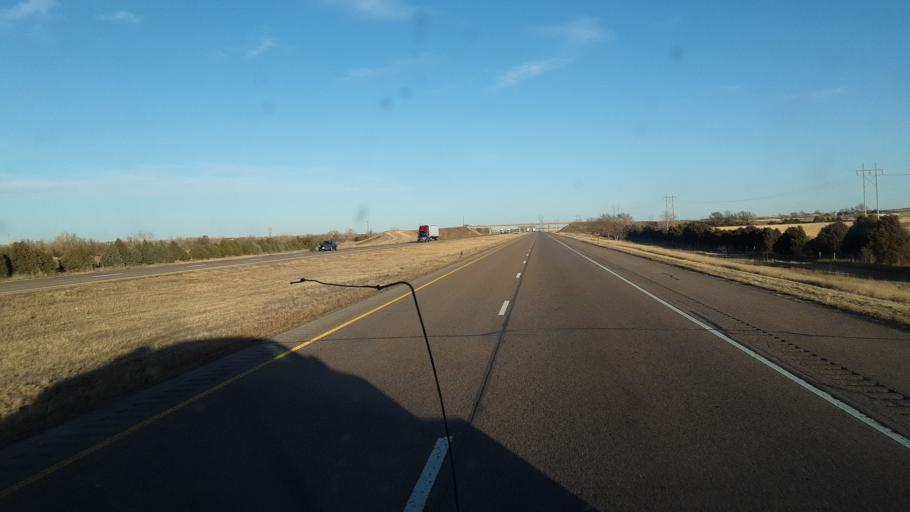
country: US
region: Nebraska
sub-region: Keith County
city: Ogallala
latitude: 41.0951
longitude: -101.8136
